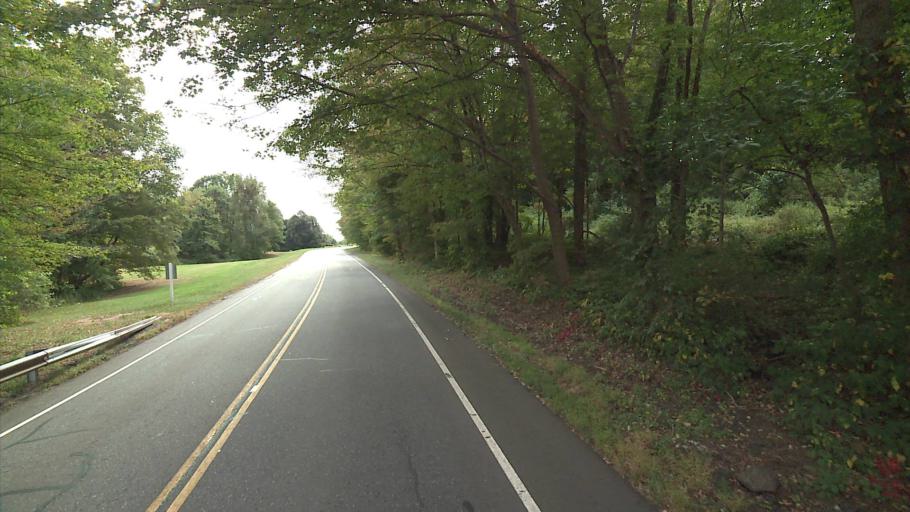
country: US
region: Connecticut
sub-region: Middlesex County
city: Durham
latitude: 41.4957
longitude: -72.7189
